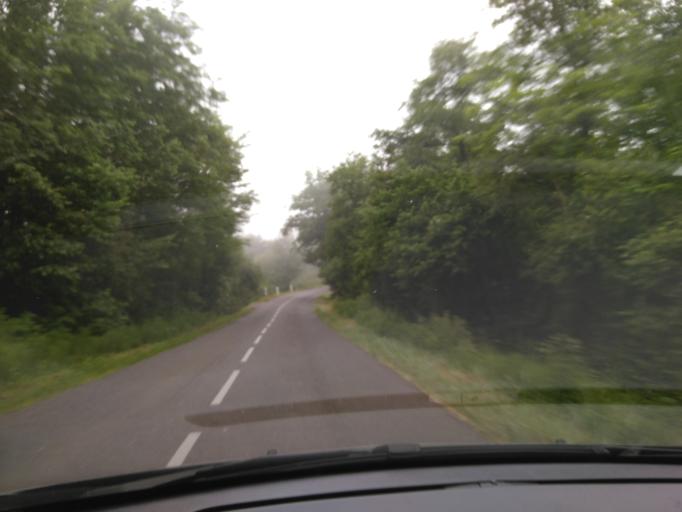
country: FR
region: Midi-Pyrenees
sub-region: Departement du Gers
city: Le Houga
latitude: 43.8612
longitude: -0.1990
